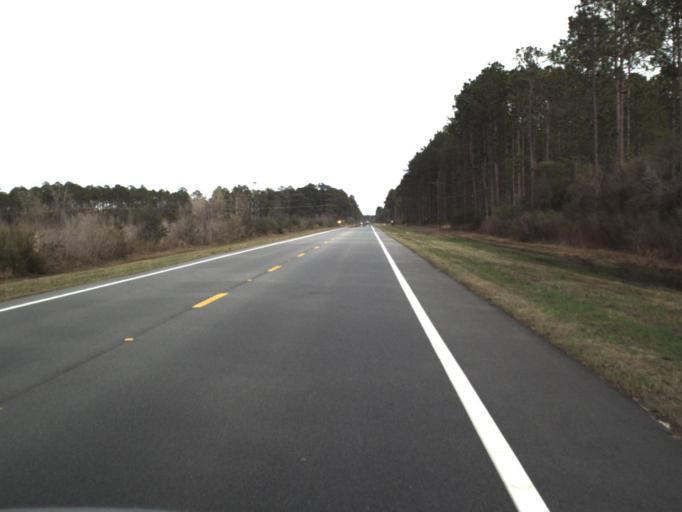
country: US
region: Florida
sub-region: Gulf County
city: Wewahitchka
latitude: 30.1418
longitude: -85.2779
